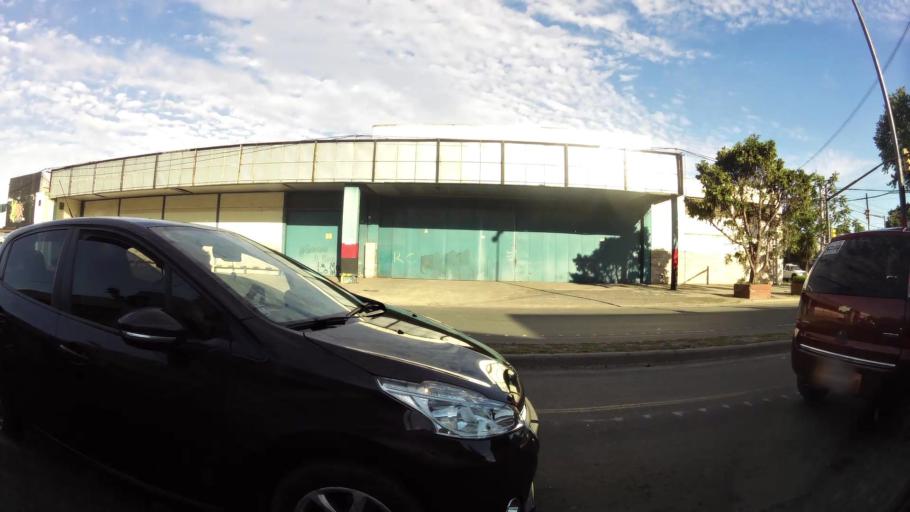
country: AR
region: Santa Fe
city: Gobernador Galvez
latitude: -32.9885
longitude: -60.6727
